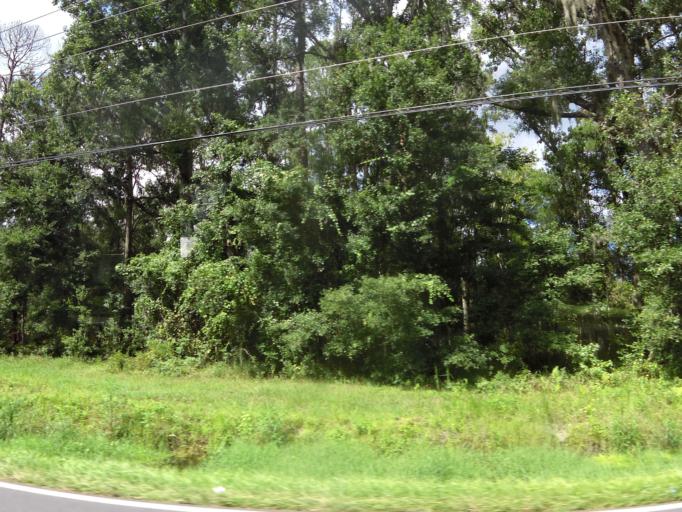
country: US
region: Florida
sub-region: Clay County
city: Green Cove Springs
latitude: 29.9412
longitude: -81.4980
